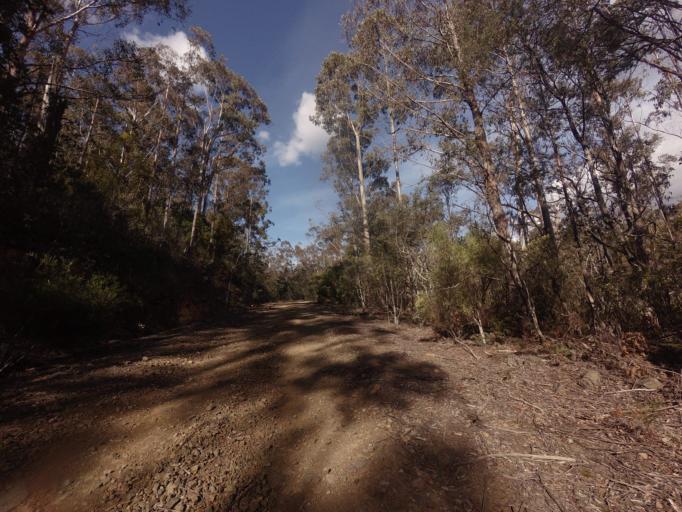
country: AU
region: Tasmania
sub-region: Break O'Day
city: St Helens
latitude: -41.8536
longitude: 148.0414
